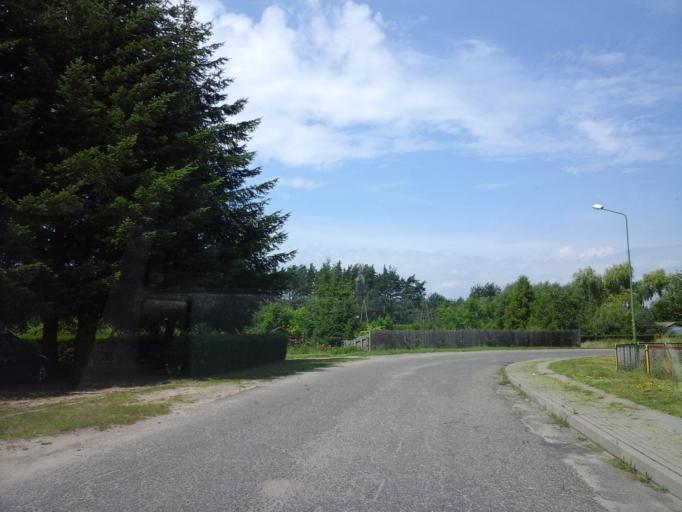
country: PL
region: West Pomeranian Voivodeship
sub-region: Powiat choszczenski
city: Bierzwnik
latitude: 53.0340
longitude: 15.6574
